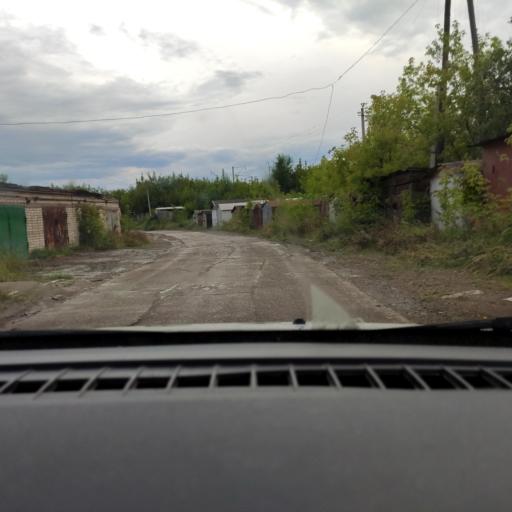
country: RU
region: Perm
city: Ferma
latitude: 57.9069
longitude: 56.2994
